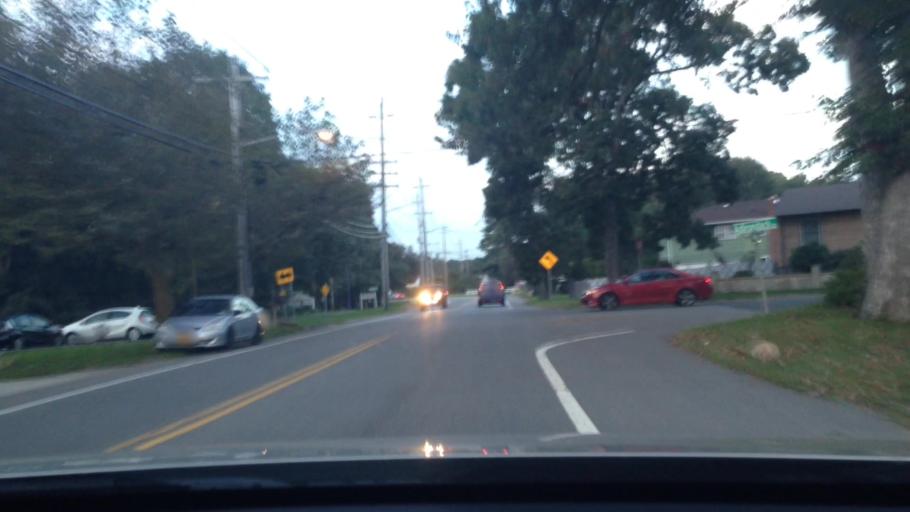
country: US
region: New York
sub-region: Suffolk County
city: Farmingville
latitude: 40.8332
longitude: -73.0248
